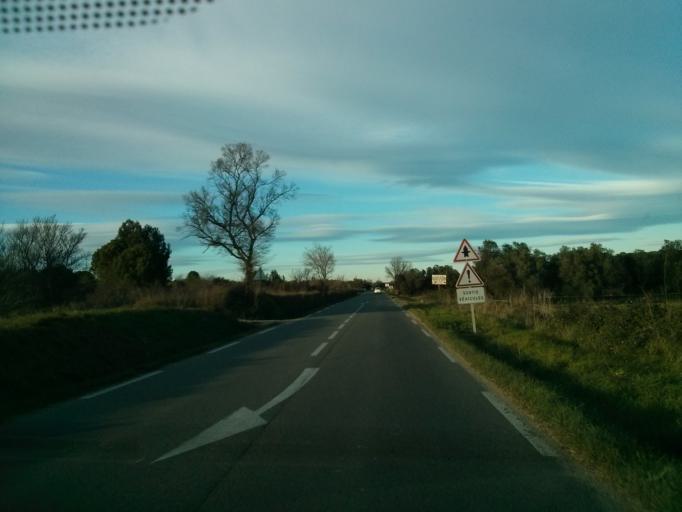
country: FR
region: Languedoc-Roussillon
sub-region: Departement du Gard
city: Mus
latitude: 43.7380
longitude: 4.2108
